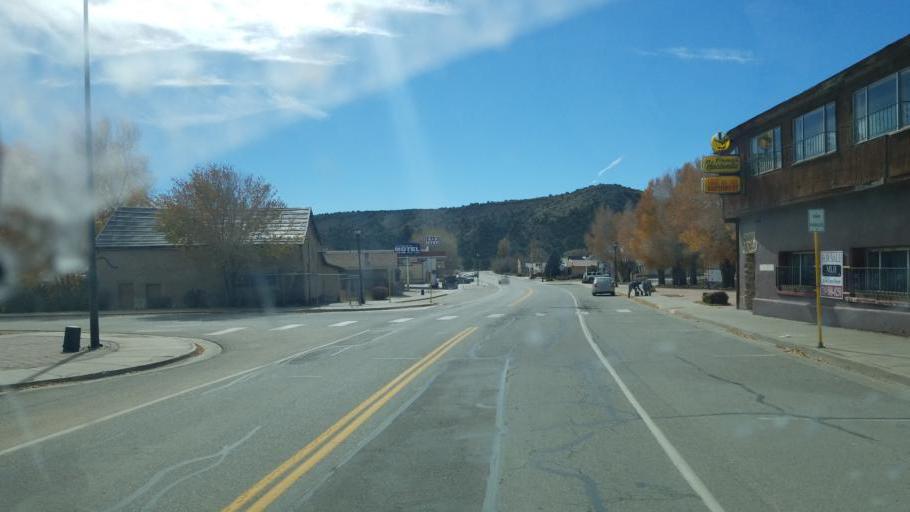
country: US
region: Colorado
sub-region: Costilla County
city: San Luis
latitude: 37.1985
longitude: -105.4265
